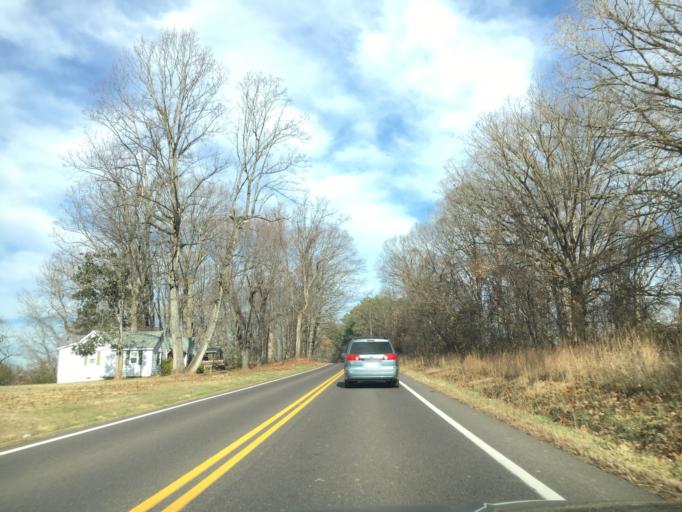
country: US
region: Virginia
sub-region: Culpeper County
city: Culpeper
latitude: 38.5177
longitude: -77.9853
